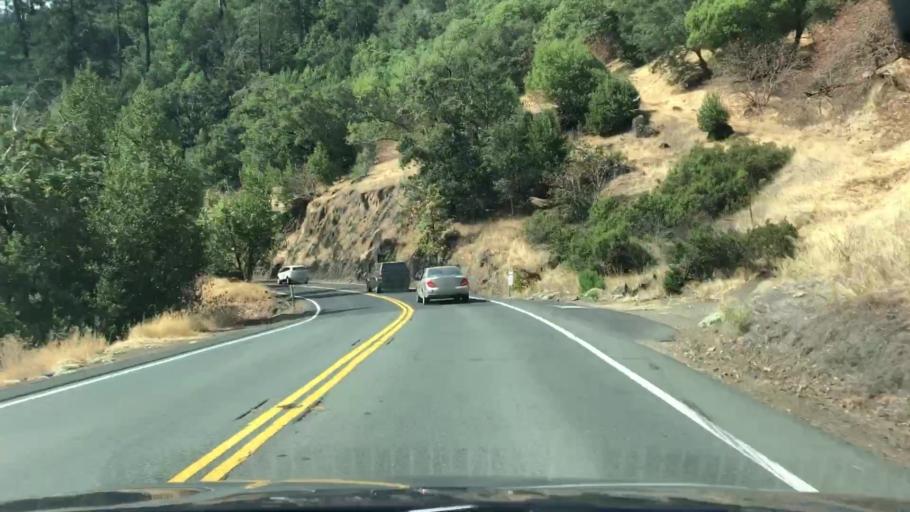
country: US
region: California
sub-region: Napa County
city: Calistoga
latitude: 38.6243
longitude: -122.5992
